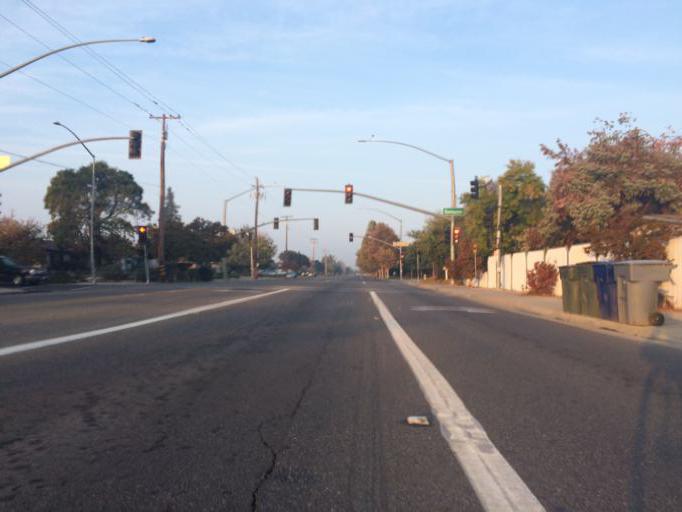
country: US
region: California
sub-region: Fresno County
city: Tarpey Village
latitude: 36.8013
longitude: -119.6911
